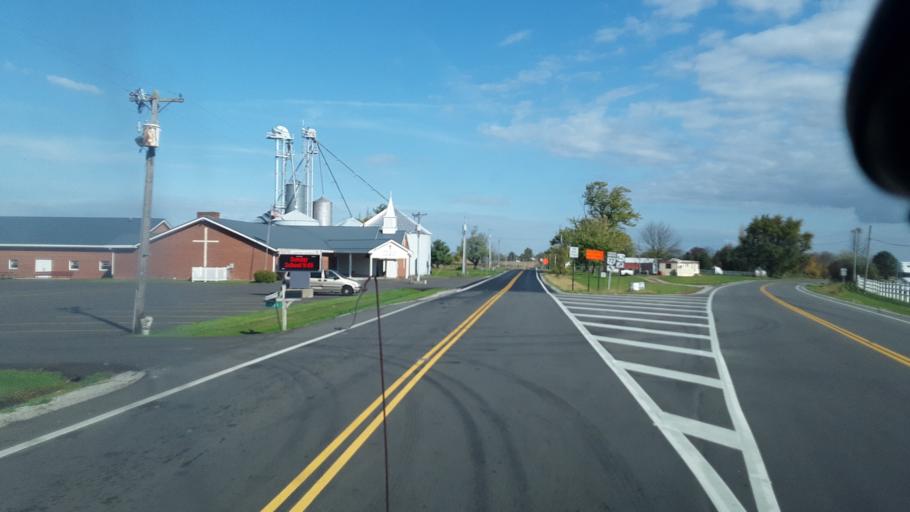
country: US
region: Ohio
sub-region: Highland County
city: Leesburg
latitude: 39.2903
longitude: -83.5910
